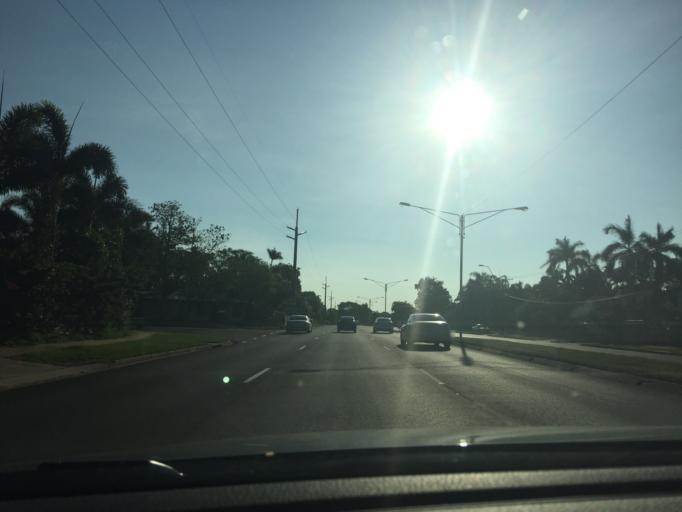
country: AU
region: Northern Territory
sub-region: Darwin
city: Nightcliff
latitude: -12.3832
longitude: 130.8740
